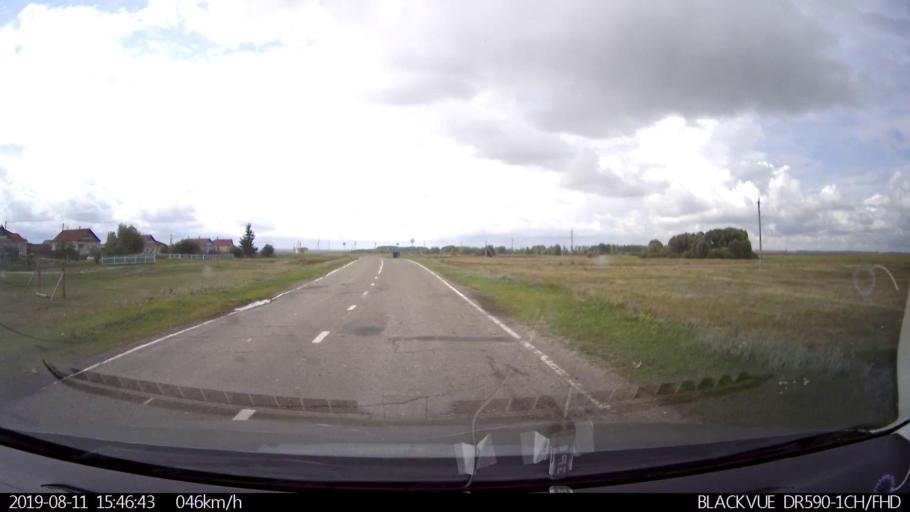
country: RU
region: Ulyanovsk
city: Ignatovka
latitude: 53.8838
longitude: 47.6547
